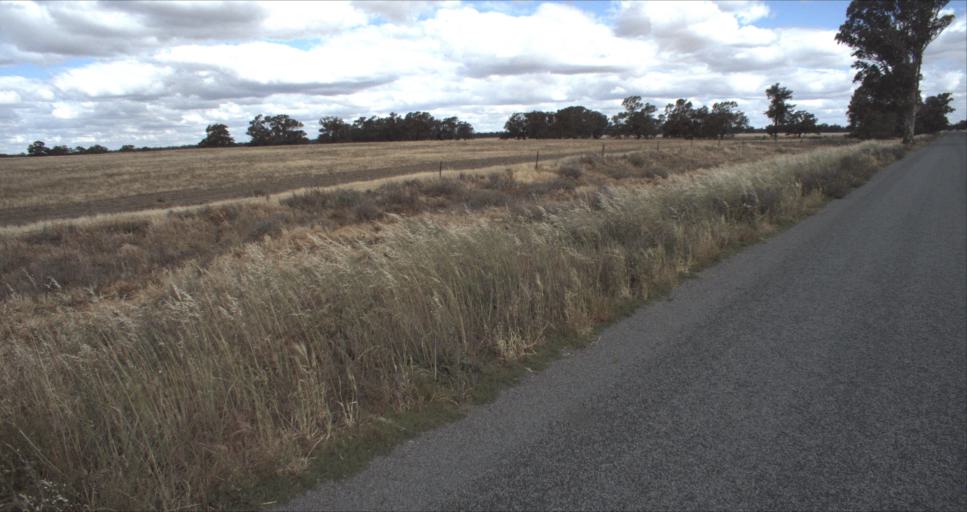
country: AU
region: New South Wales
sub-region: Leeton
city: Leeton
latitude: -34.6890
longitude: 146.3441
